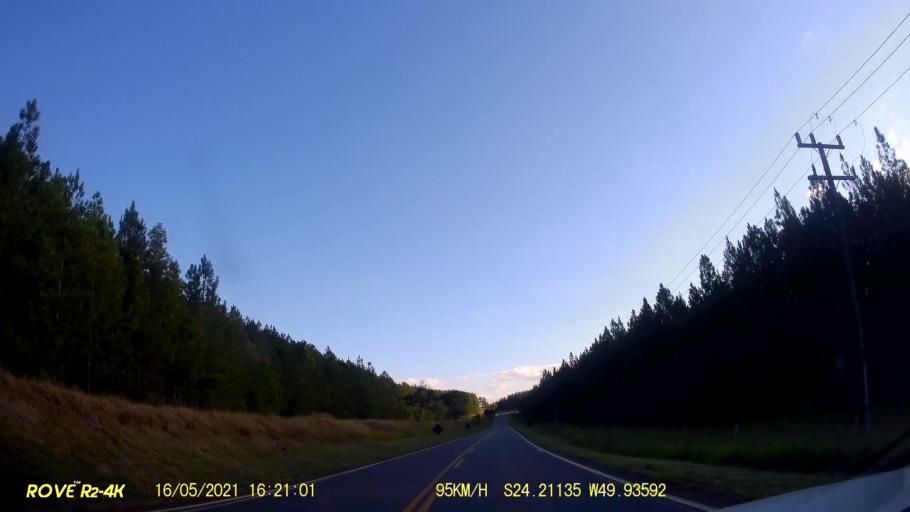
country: BR
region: Parana
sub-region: Jaguariaiva
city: Jaguariaiva
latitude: -24.2115
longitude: -49.9361
